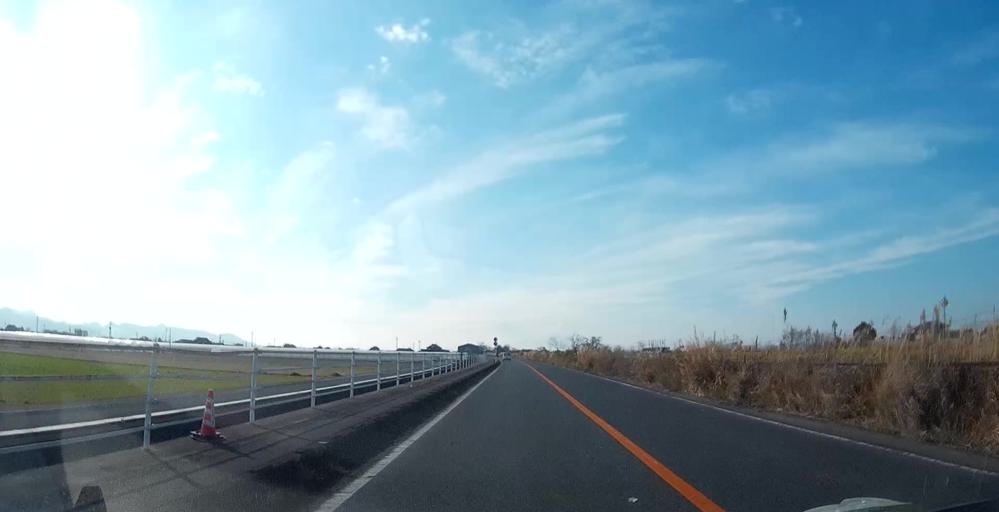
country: JP
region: Kumamoto
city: Uto
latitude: 32.7328
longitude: 130.6569
